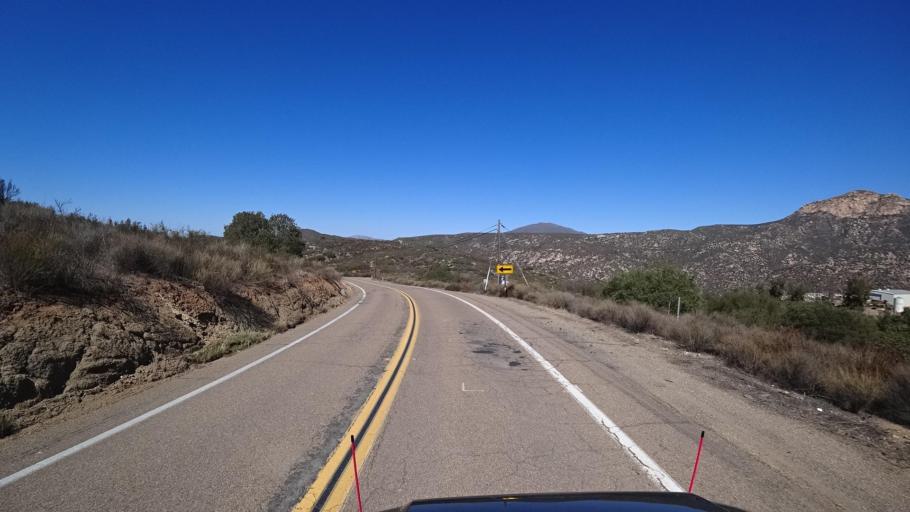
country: US
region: California
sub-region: San Diego County
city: Alpine
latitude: 32.7850
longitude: -116.7212
